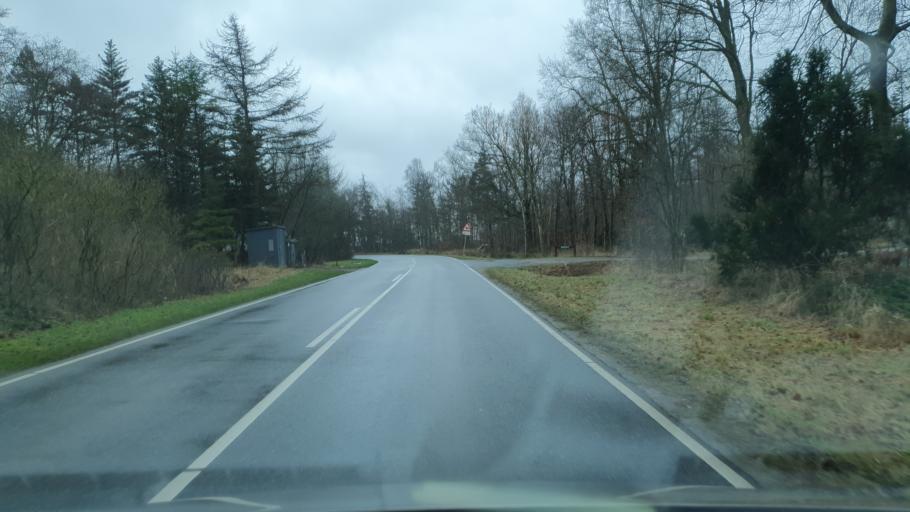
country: DK
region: North Denmark
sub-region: Jammerbugt Kommune
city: Fjerritslev
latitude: 57.1204
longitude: 9.1263
